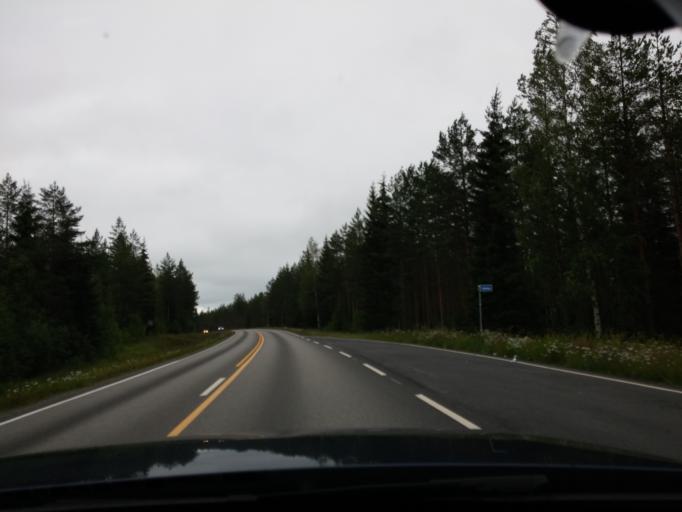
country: FI
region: Central Finland
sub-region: Saarijaervi-Viitasaari
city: Saarijaervi
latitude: 62.6784
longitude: 25.2204
